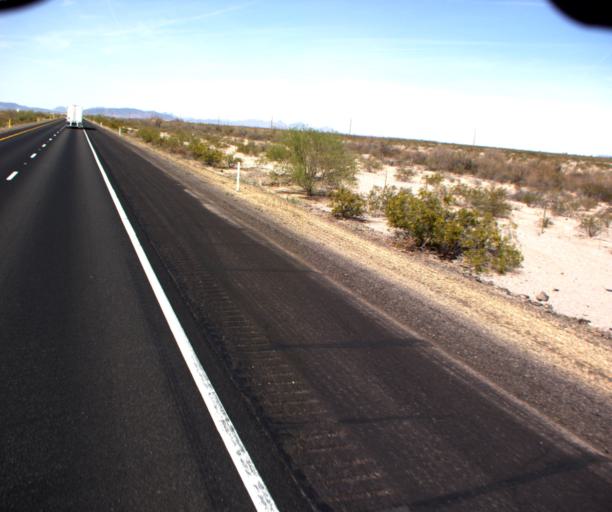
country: US
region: Arizona
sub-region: La Paz County
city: Salome
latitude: 33.6224
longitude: -113.7074
